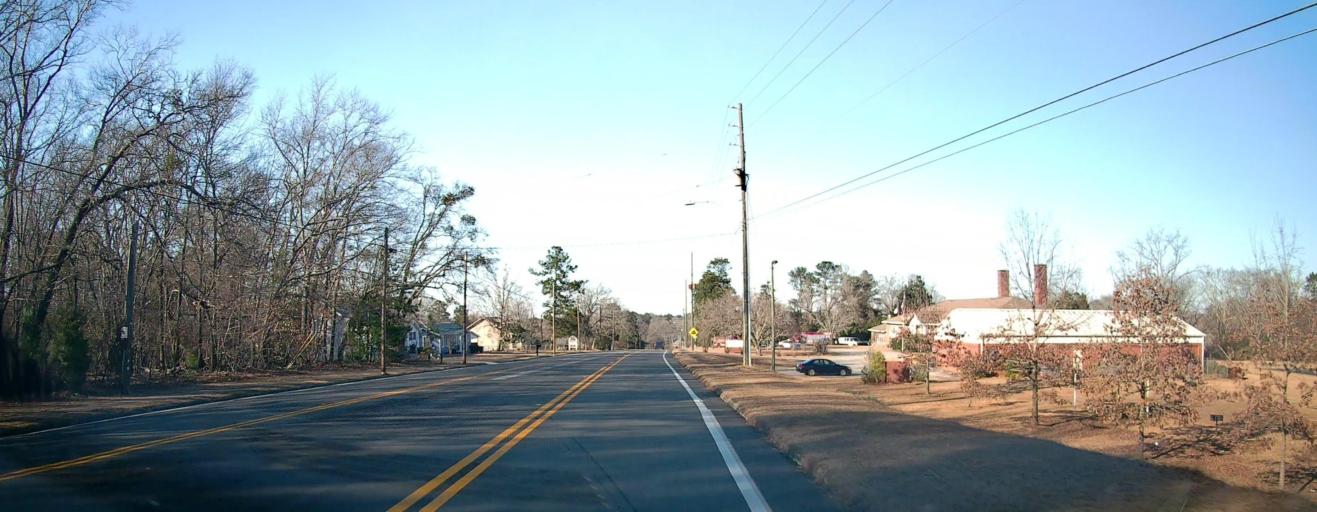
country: US
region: Georgia
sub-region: Meriwether County
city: Manchester
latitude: 32.8859
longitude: -84.6809
